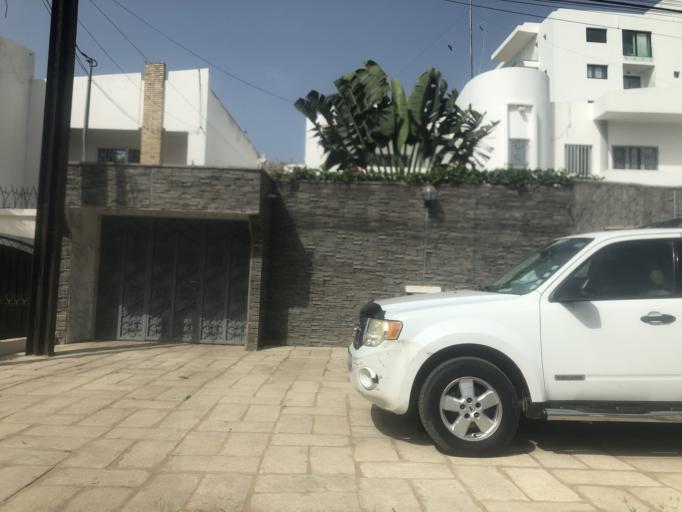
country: SN
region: Dakar
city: Mermoz Boabab
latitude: 14.7388
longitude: -17.5136
